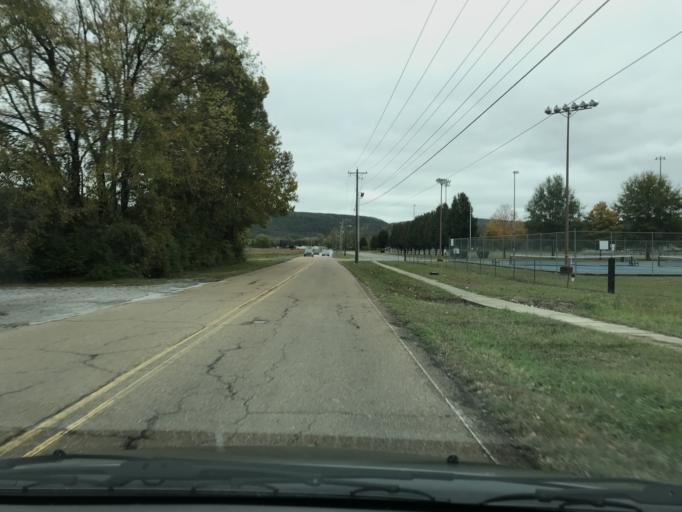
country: US
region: Tennessee
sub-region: Rhea County
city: Dayton
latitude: 35.4925
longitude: -85.0232
